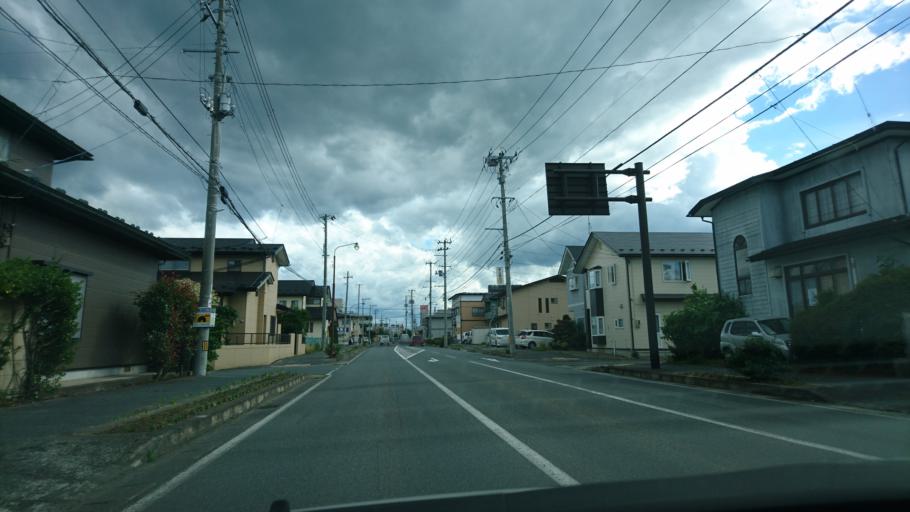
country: JP
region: Iwate
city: Kitakami
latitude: 39.2943
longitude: 141.1207
